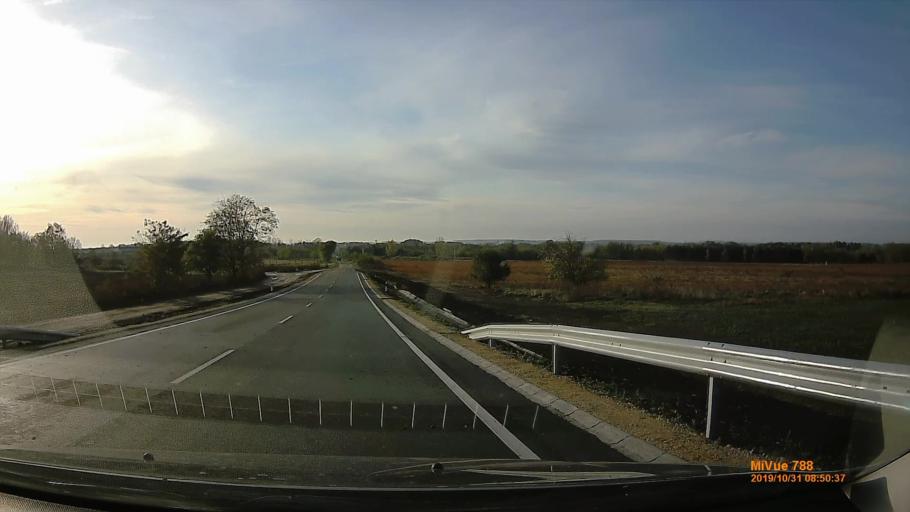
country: HU
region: Pest
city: Albertirsa
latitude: 47.2695
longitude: 19.6045
